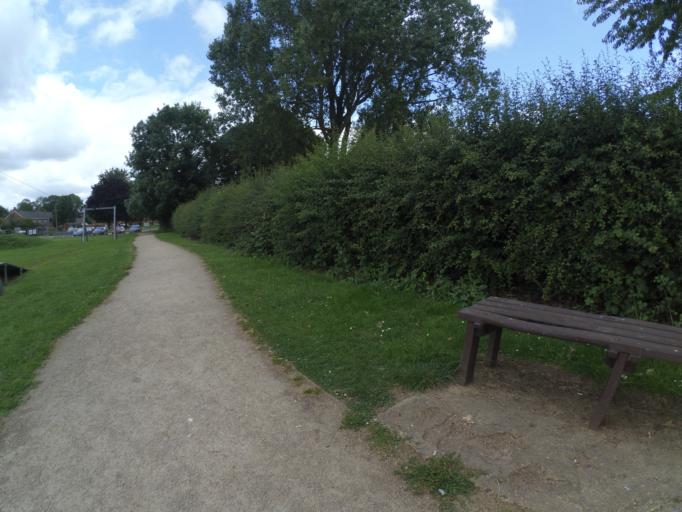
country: GB
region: England
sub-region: Warwickshire
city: Long Lawford
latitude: 52.3807
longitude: -1.3036
